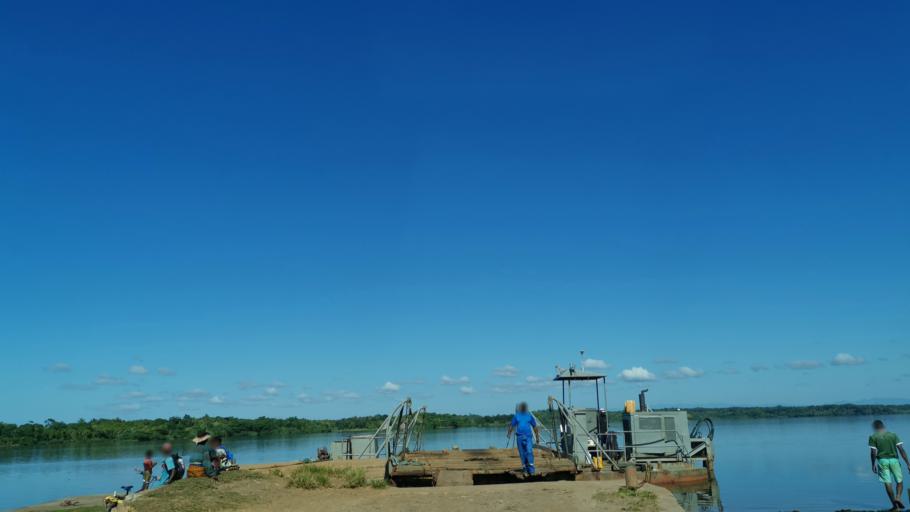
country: MG
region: Atsimo-Atsinanana
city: Vohipaho
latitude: -23.5991
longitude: 47.6117
